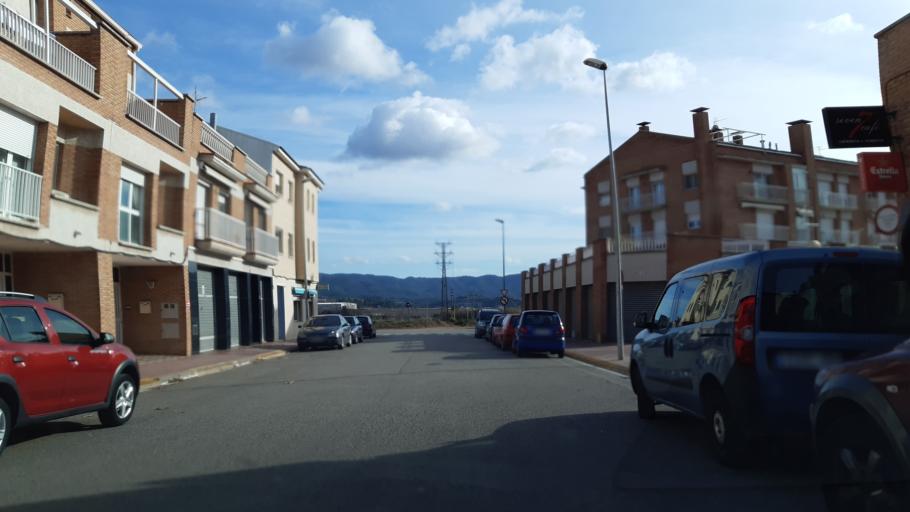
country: ES
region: Catalonia
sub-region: Provincia de Barcelona
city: Vilanova del Cami
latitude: 41.5694
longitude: 1.6430
